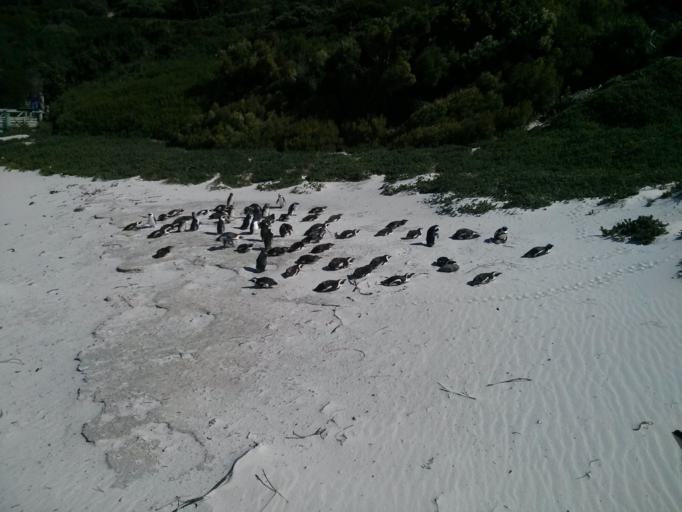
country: ZA
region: Western Cape
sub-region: City of Cape Town
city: Retreat
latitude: -34.3228
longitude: 18.4634
